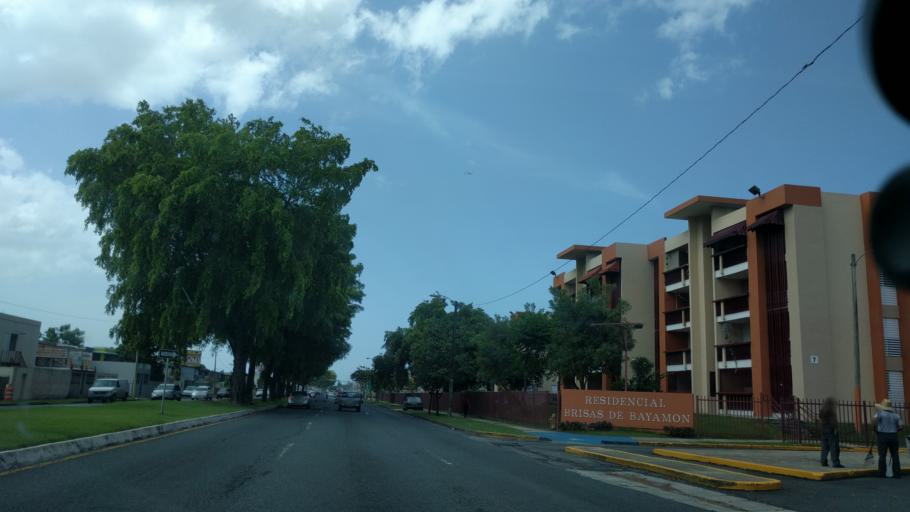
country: PR
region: Bayamon
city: Bayamon
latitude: 18.4135
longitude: -66.1608
